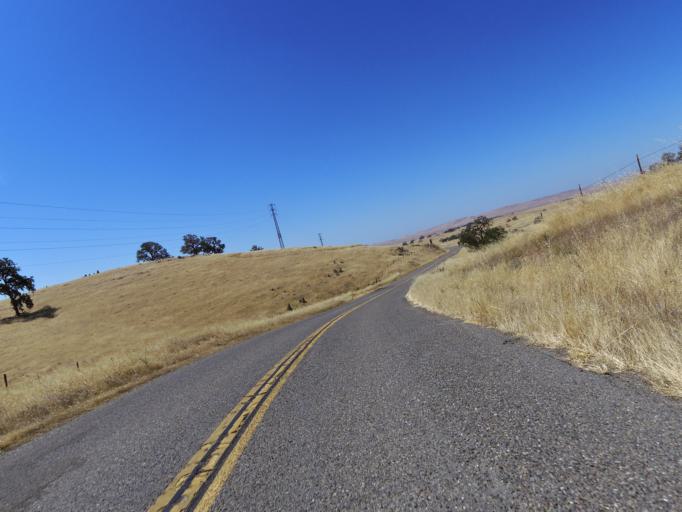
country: US
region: California
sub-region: Merced County
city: Planada
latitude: 37.5504
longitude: -120.3254
